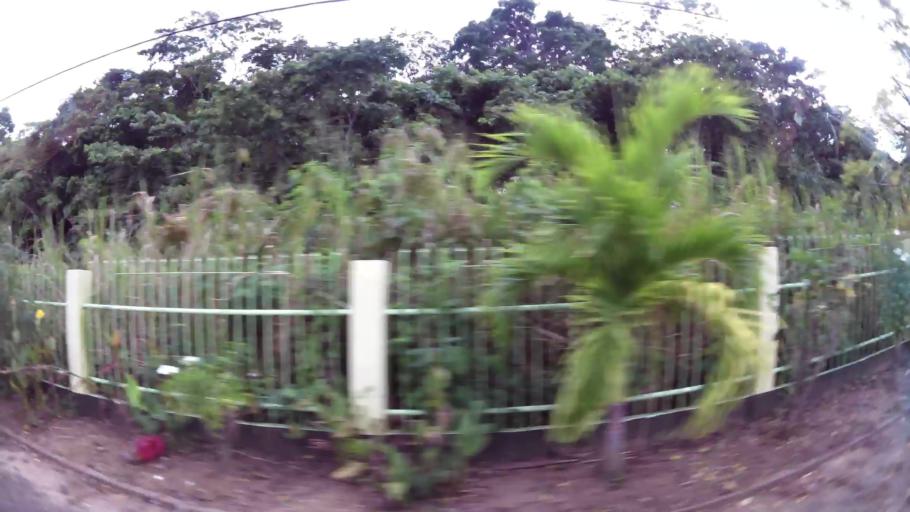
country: SR
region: Paramaribo
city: Paramaribo
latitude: 5.8657
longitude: -55.1768
